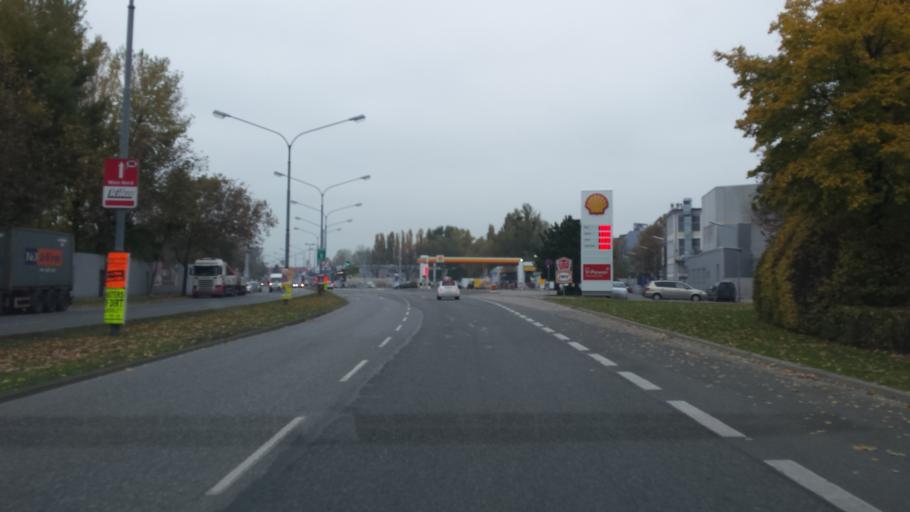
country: AT
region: Lower Austria
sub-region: Politischer Bezirk Wien-Umgebung
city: Gerasdorf bei Wien
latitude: 48.2257
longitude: 16.4450
